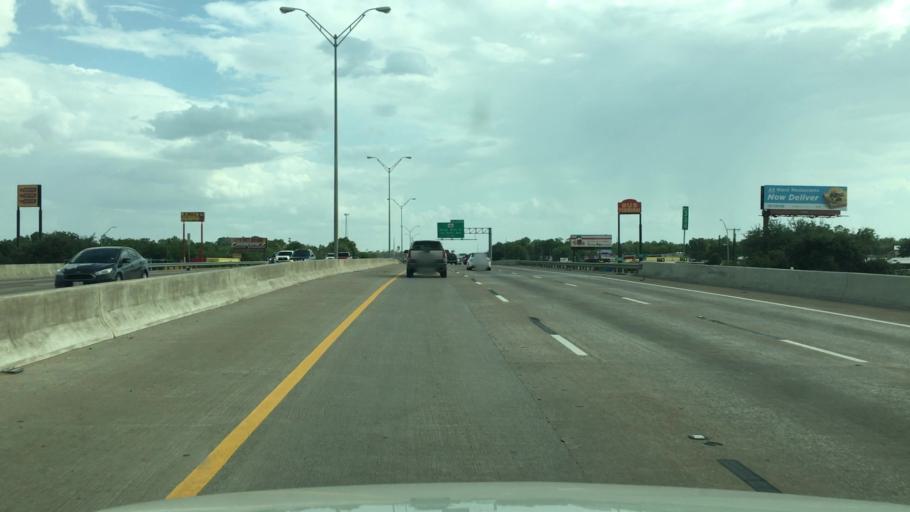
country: US
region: Texas
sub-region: McLennan County
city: Beverly
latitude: 31.5361
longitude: -97.1295
